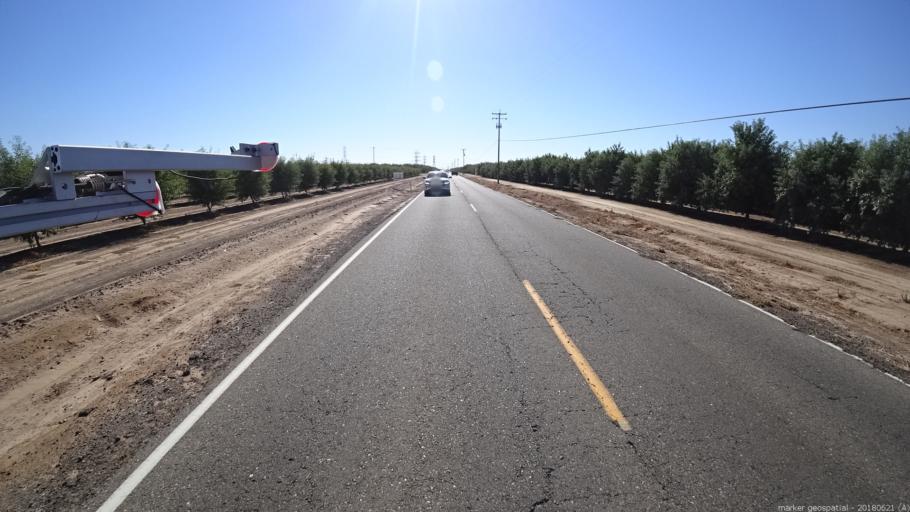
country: US
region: California
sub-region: Fresno County
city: Biola
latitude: 36.8514
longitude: -119.9263
